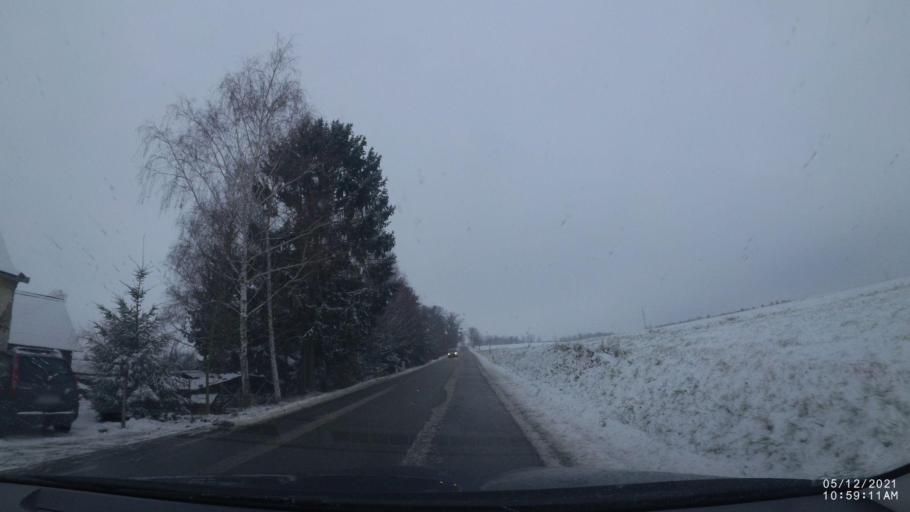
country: CZ
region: Kralovehradecky
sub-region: Okres Rychnov nad Kneznou
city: Rychnov nad Kneznou
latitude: 50.1640
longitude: 16.2381
